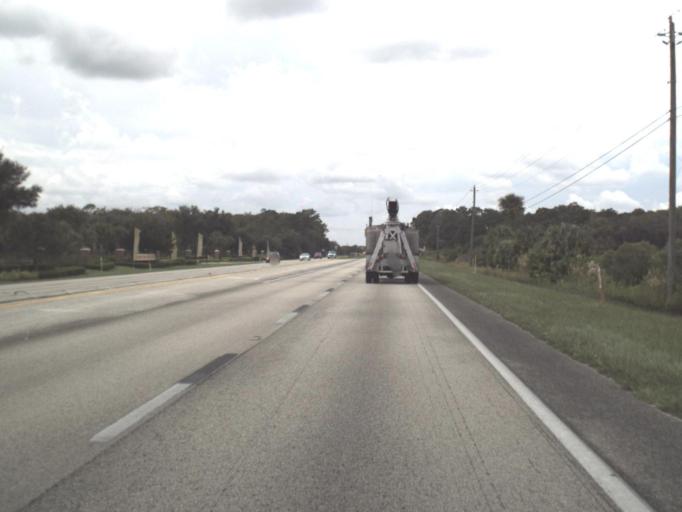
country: US
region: Florida
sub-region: Lee County
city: Olga
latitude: 26.7129
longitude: -81.7063
